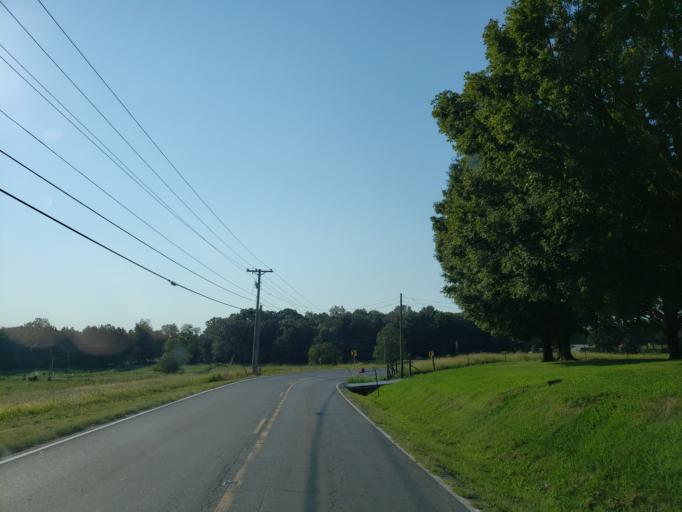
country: US
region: Tennessee
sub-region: Bradley County
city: Wildwood Lake
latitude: 35.0969
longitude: -84.8072
